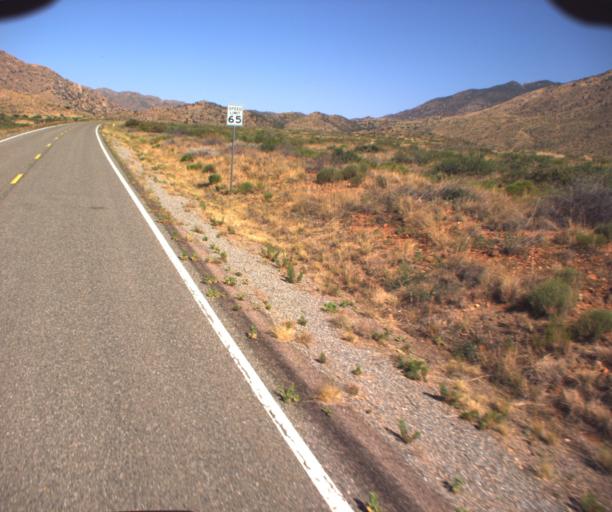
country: US
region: Arizona
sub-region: Graham County
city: Swift Trail Junction
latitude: 32.5604
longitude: -109.7694
